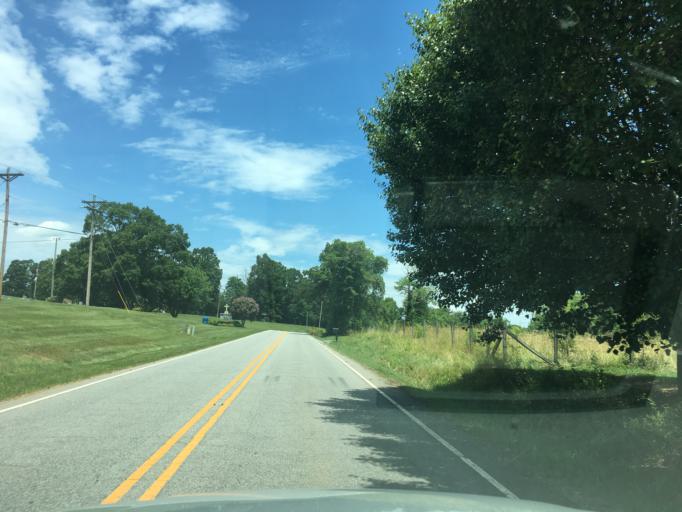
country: US
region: North Carolina
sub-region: Burke County
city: Glen Alpine
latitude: 35.6715
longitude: -81.7696
